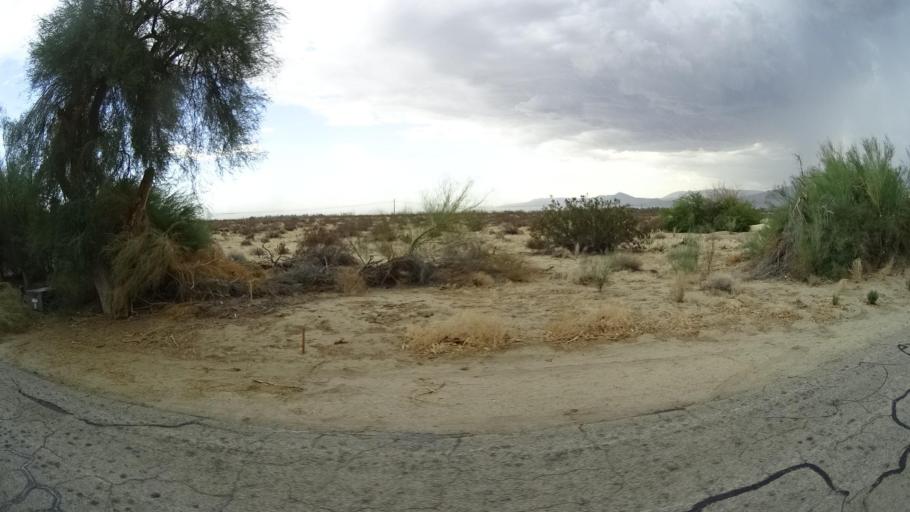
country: US
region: California
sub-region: San Diego County
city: Borrego Springs
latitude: 33.2866
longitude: -116.3855
